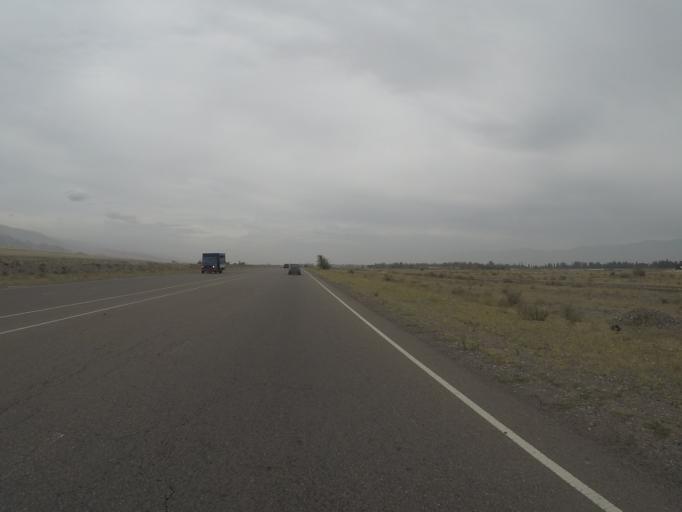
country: KG
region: Chuy
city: Bystrovka
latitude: 42.8300
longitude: 75.5169
